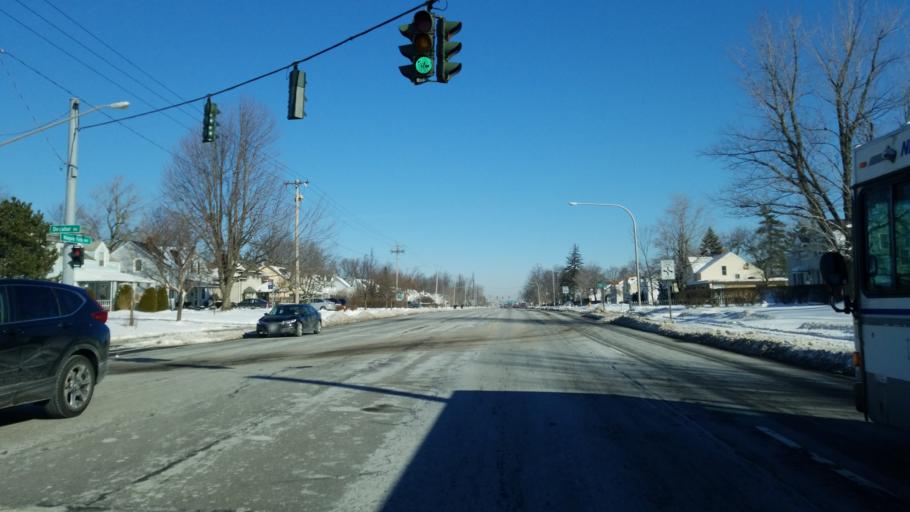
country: US
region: New York
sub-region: Erie County
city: Eggertsville
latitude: 42.9690
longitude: -78.8234
